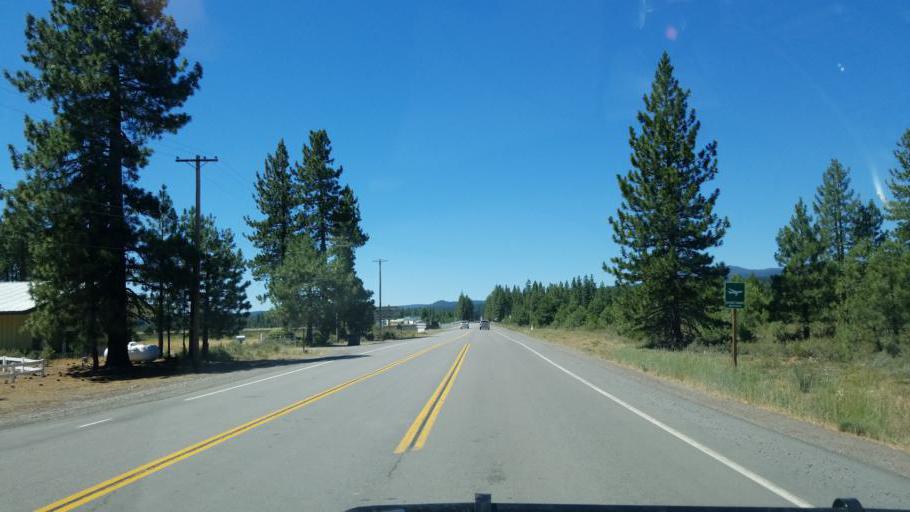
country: US
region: California
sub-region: Plumas County
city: Chester
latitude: 40.2943
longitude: -121.2414
